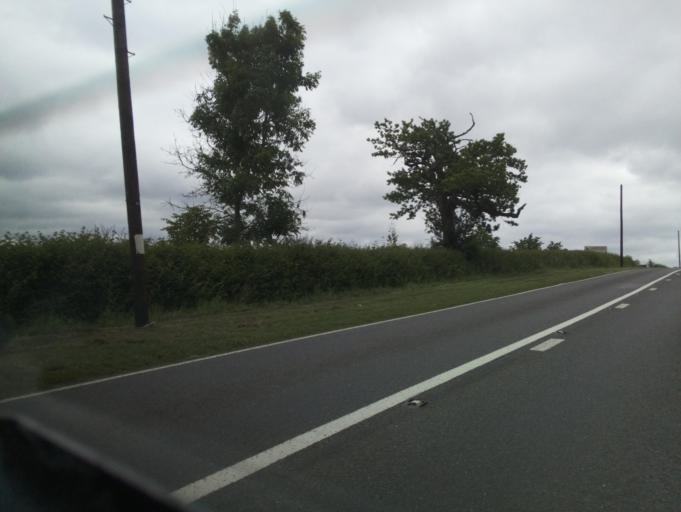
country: GB
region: England
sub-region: Leicestershire
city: Grimston
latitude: 52.8039
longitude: -1.0614
